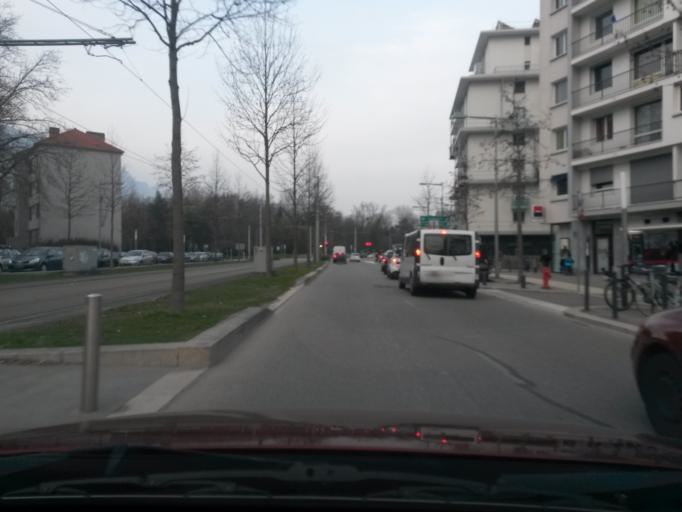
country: FR
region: Rhone-Alpes
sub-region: Departement de l'Isere
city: La Tronche
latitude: 45.1873
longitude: 5.7450
